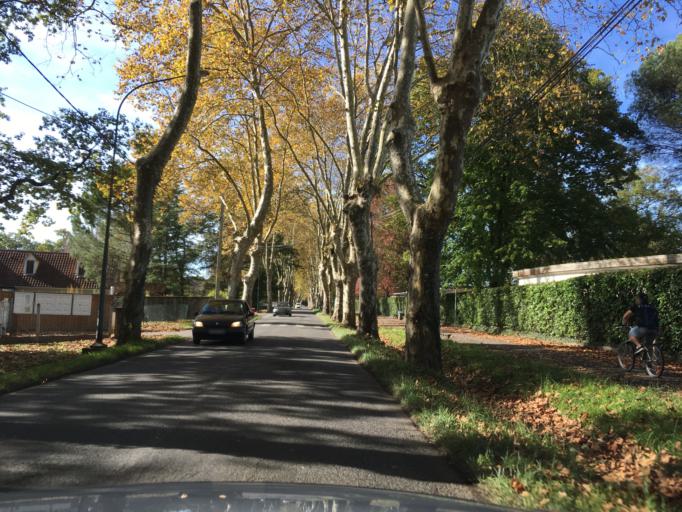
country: FR
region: Aquitaine
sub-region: Departement des Pyrenees-Atlantiques
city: Lons
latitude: 43.3335
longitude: -0.3712
